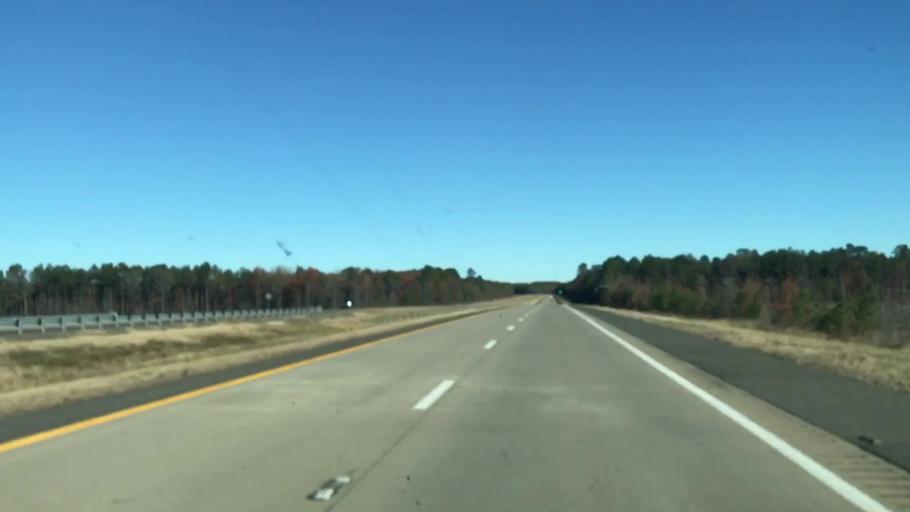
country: US
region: Texas
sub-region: Bowie County
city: Texarkana
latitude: 33.2253
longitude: -93.8732
